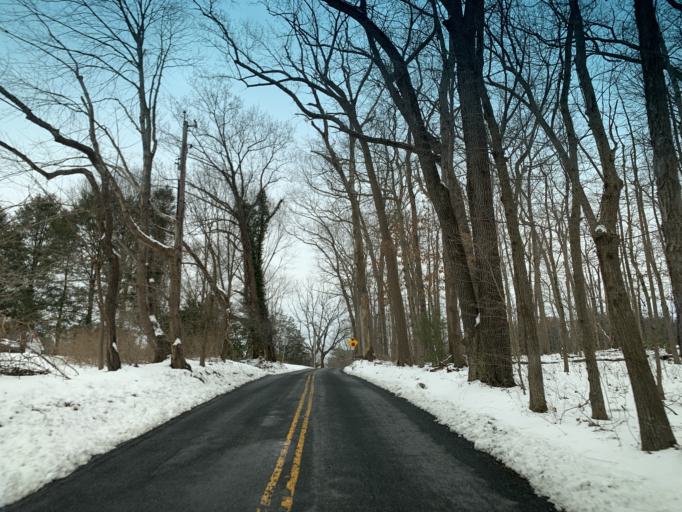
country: US
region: Maryland
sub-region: Harford County
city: Jarrettsville
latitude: 39.5812
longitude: -76.4814
